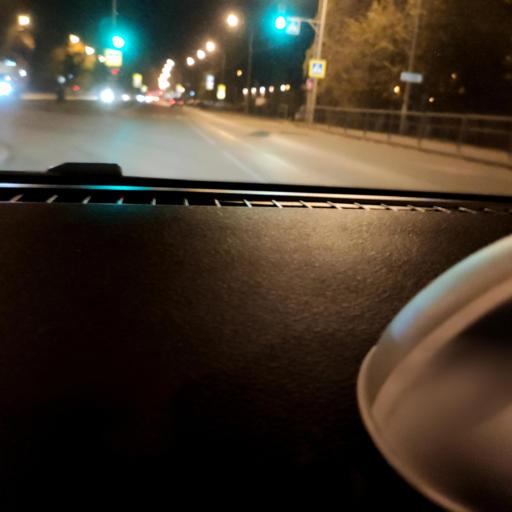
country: RU
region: Samara
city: Smyshlyayevka
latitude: 53.2107
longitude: 50.2865
